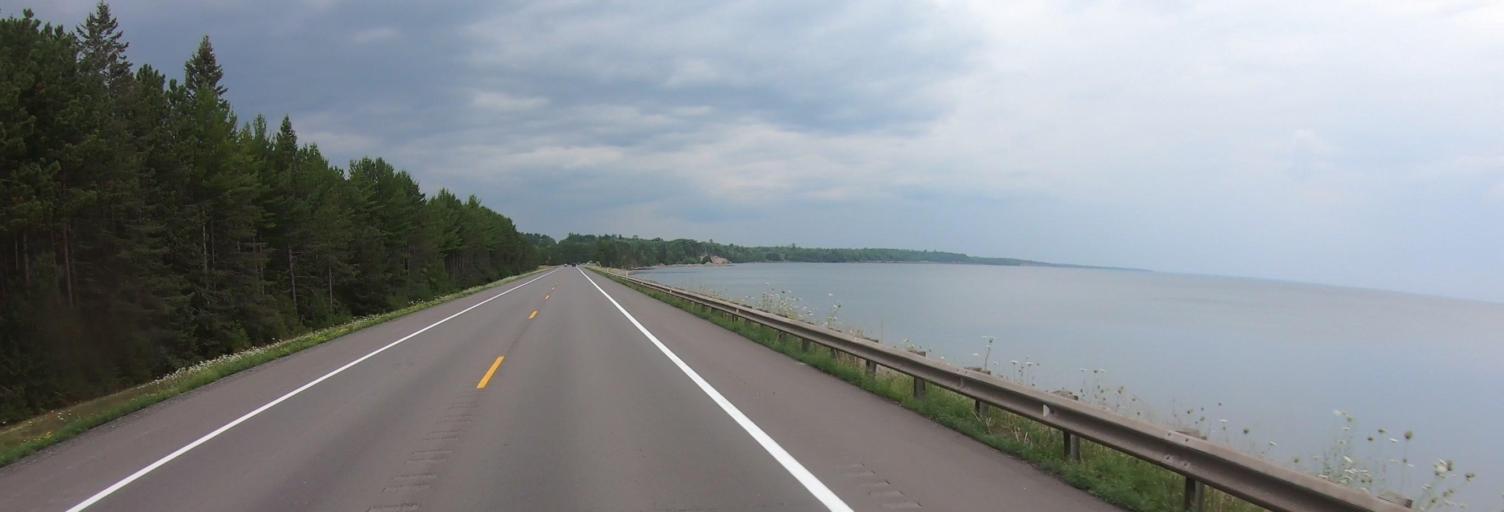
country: US
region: Michigan
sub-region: Baraga County
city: Baraga
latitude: 46.8160
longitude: -88.4769
